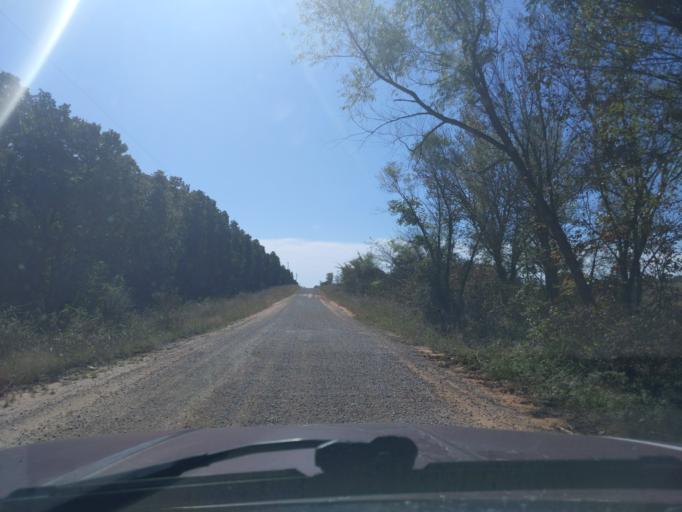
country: US
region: Oklahoma
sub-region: Creek County
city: Bristow
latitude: 35.6745
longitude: -96.4233
